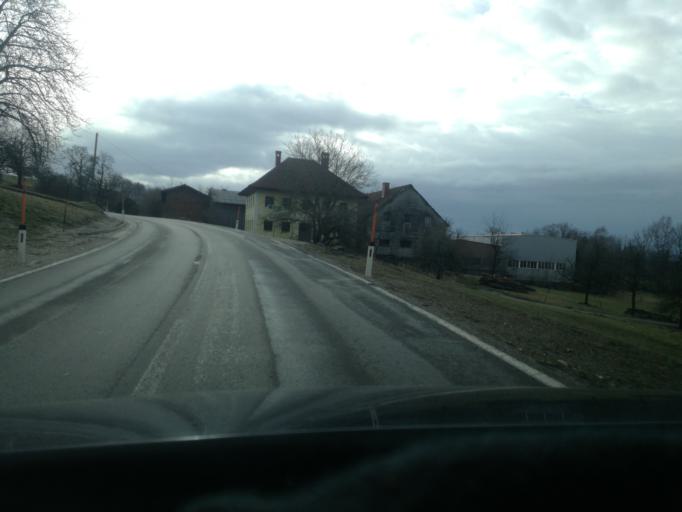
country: AT
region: Upper Austria
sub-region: Politischer Bezirk Vocklabruck
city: Frankenburg
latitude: 48.0815
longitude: 13.4844
